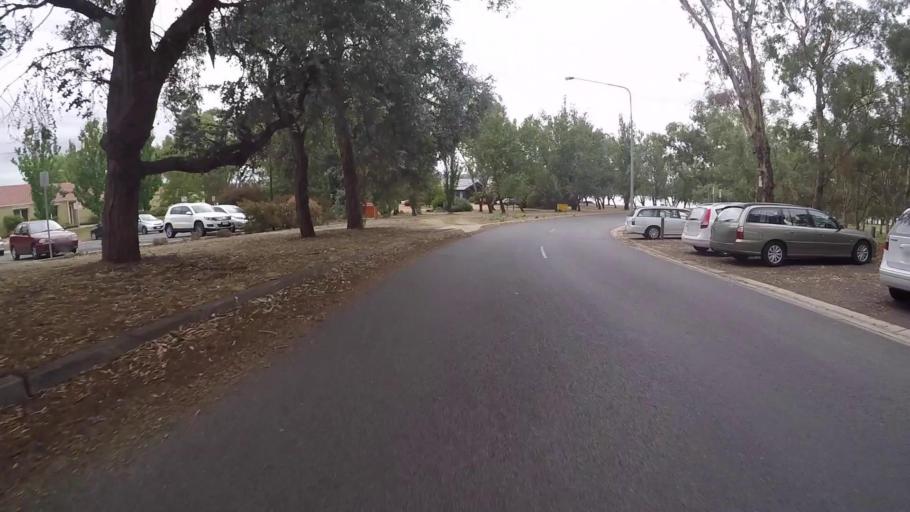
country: AU
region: Australian Capital Territory
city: Forrest
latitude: -35.3037
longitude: 149.1514
